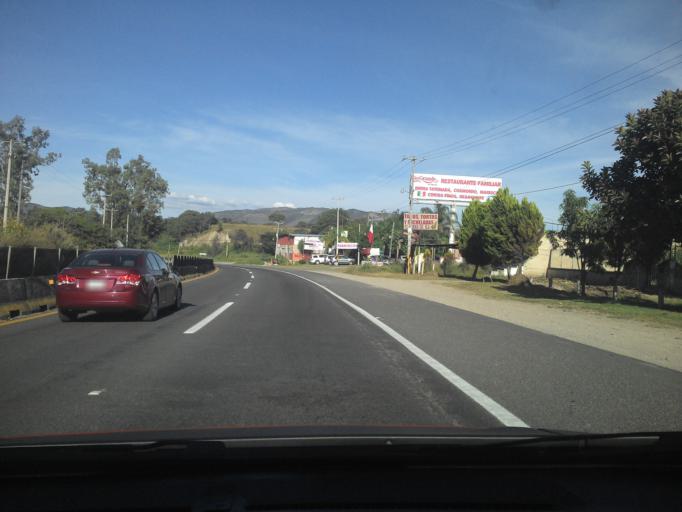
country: MX
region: Jalisco
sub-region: Tala
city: Los Ruisenores
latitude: 20.7209
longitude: -103.6245
